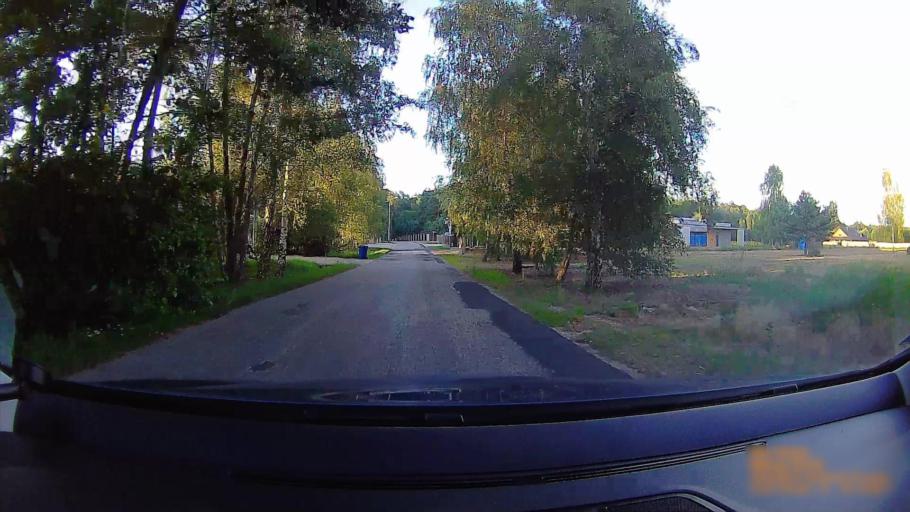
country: PL
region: Greater Poland Voivodeship
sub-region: Konin
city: Konin
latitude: 52.2024
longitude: 18.3221
